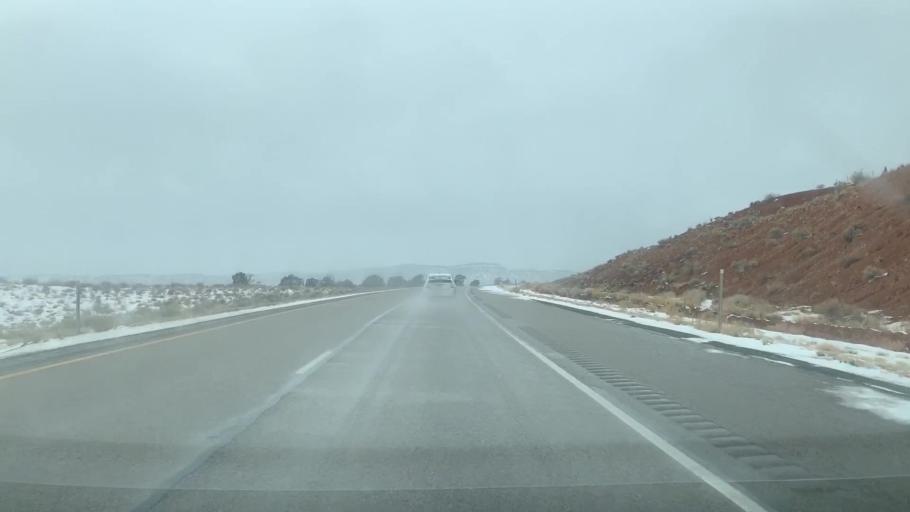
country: US
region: Utah
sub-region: Emery County
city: Castle Dale
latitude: 38.8674
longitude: -110.7118
